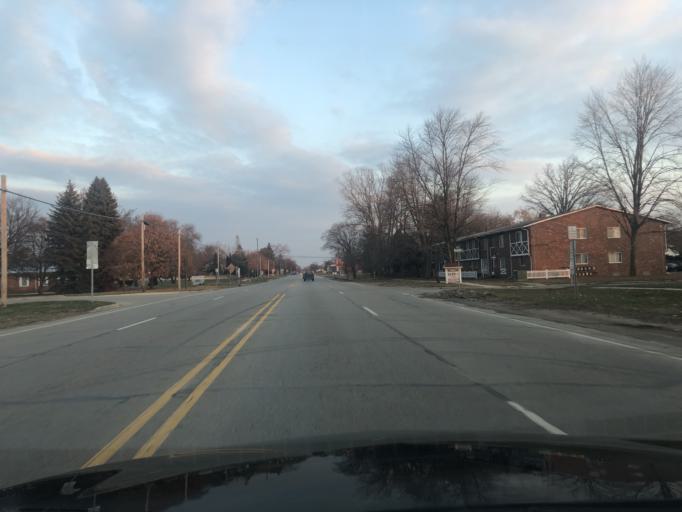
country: US
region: Michigan
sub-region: Wayne County
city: Romulus
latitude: 42.2337
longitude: -83.3858
